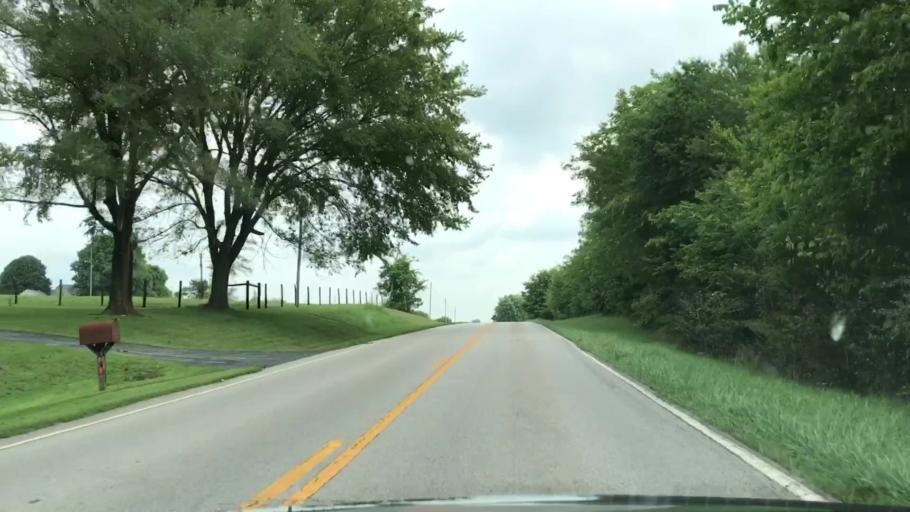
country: US
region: Kentucky
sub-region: Barren County
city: Cave City
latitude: 37.0997
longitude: -86.0061
